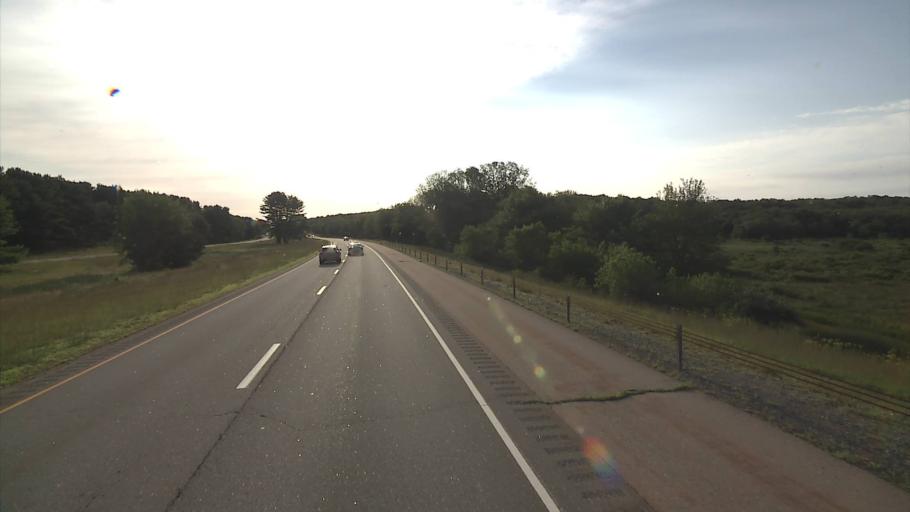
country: US
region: Connecticut
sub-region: New London County
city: Colchester
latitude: 41.5652
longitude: -72.2423
